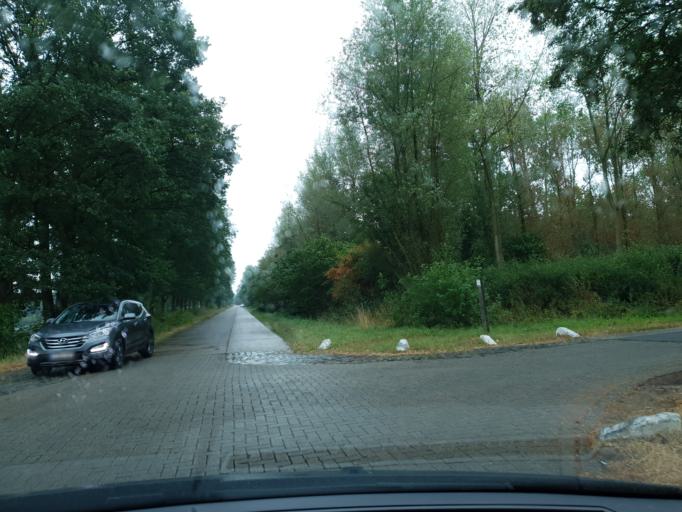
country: BE
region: Flanders
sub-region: Provincie Antwerpen
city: Beerse
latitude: 51.3362
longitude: 4.8442
